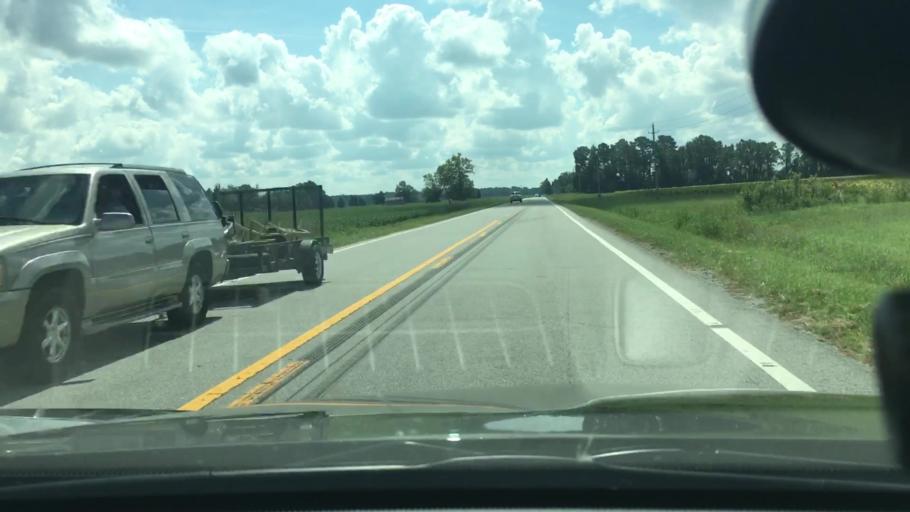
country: US
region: North Carolina
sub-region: Pitt County
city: Summerfield
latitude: 35.6668
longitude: -77.4783
